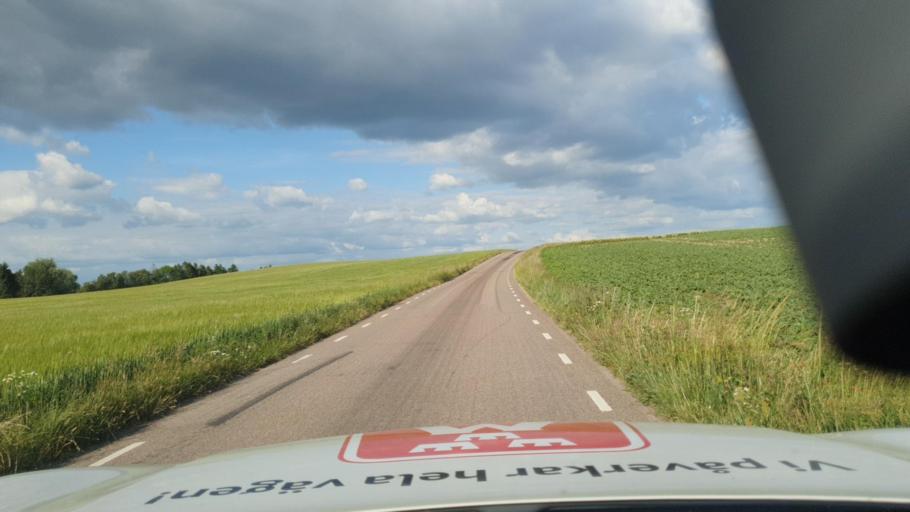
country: SE
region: Skane
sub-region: Skurups Kommun
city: Rydsgard
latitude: 55.4453
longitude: 13.6952
